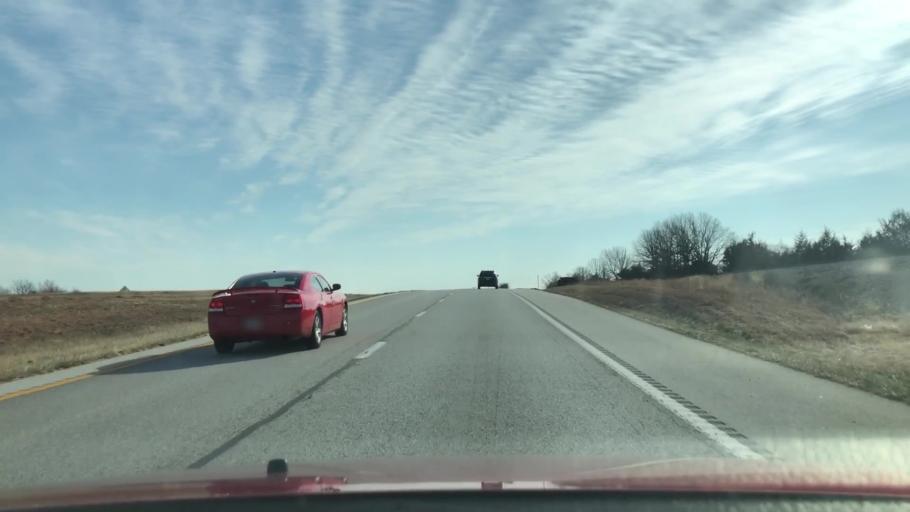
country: US
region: Missouri
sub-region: Webster County
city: Seymour
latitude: 37.1200
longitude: -92.6962
